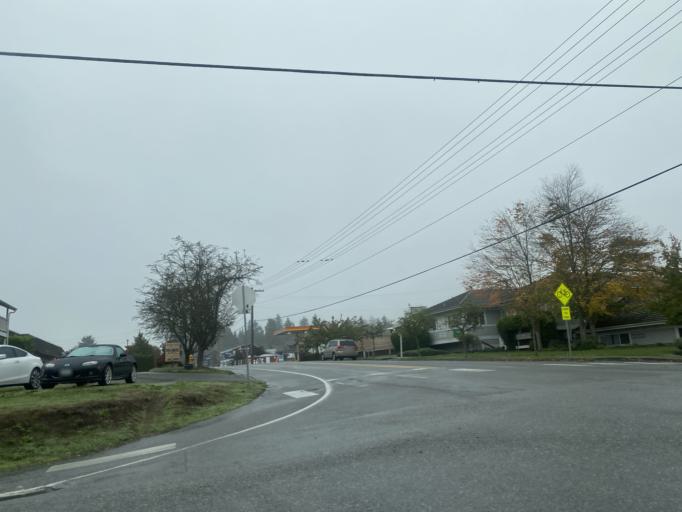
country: US
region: Washington
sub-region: Island County
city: Freeland
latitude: 48.0097
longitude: -122.5272
